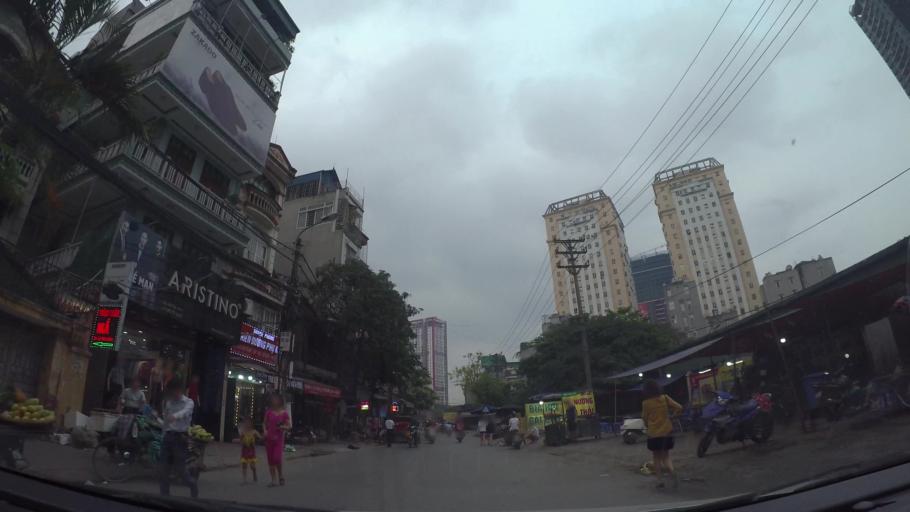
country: VN
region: Ha Noi
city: Cau Dien
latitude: 21.0314
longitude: 105.7778
